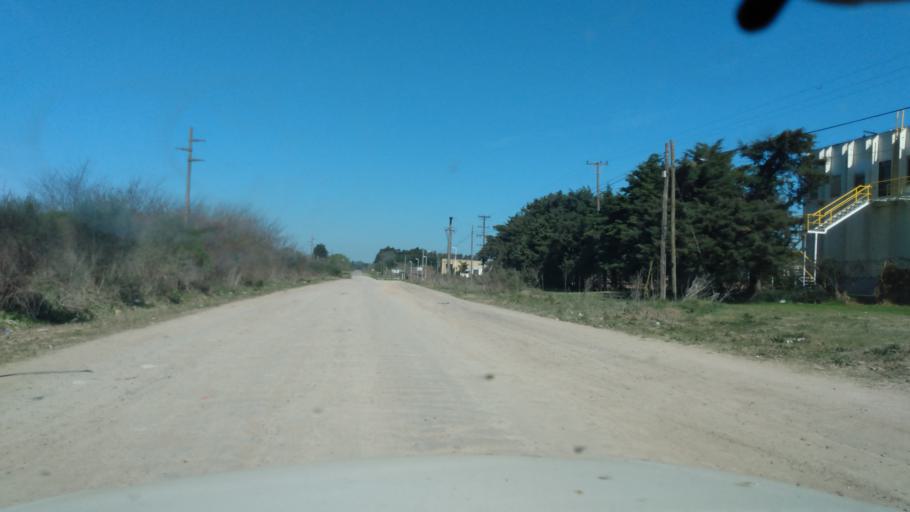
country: AR
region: Buenos Aires
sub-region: Partido de Lujan
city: Lujan
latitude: -34.5655
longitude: -59.1408
